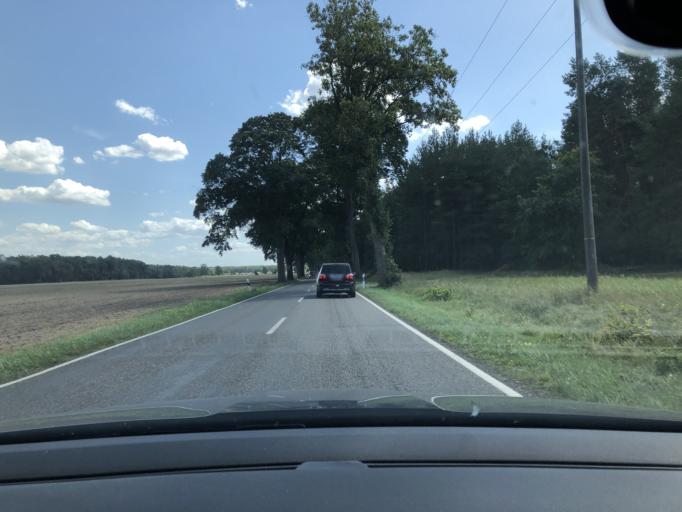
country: DE
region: Brandenburg
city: Ruthnick
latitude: 52.8913
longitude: 12.9869
